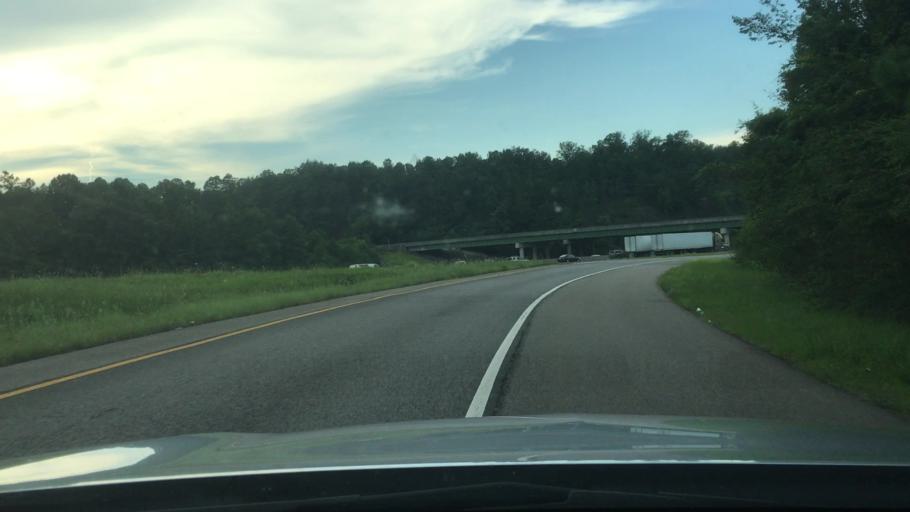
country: US
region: Alabama
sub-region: Jefferson County
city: Irondale
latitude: 33.5468
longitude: -86.6413
